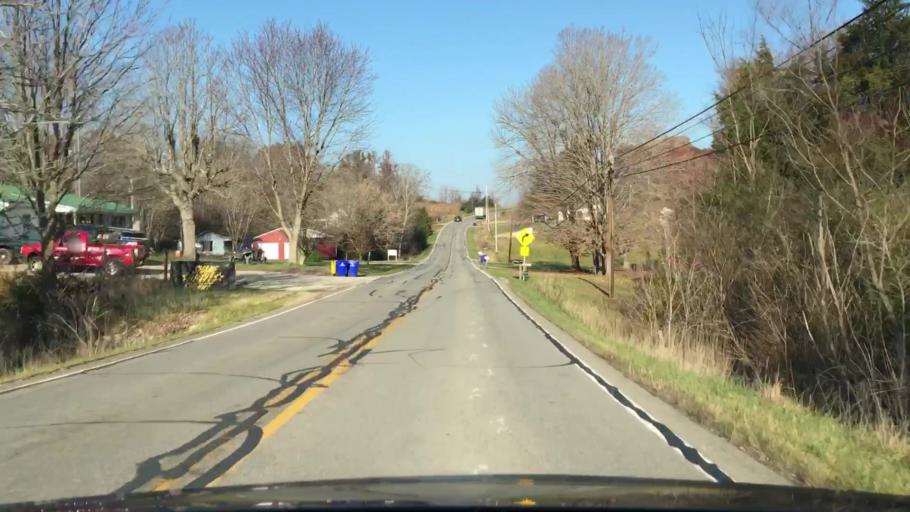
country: US
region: Kentucky
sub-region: Edmonson County
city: Brownsville
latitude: 37.2216
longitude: -86.2944
